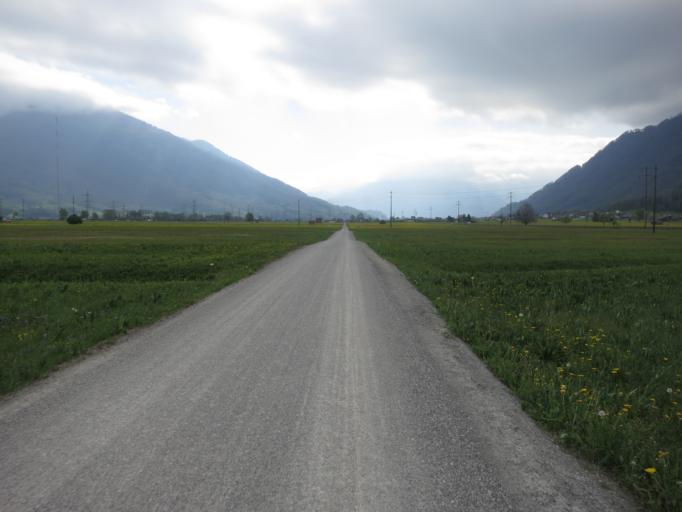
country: CH
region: Glarus
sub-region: Glarus
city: Bilten
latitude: 47.1639
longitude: 9.0086
